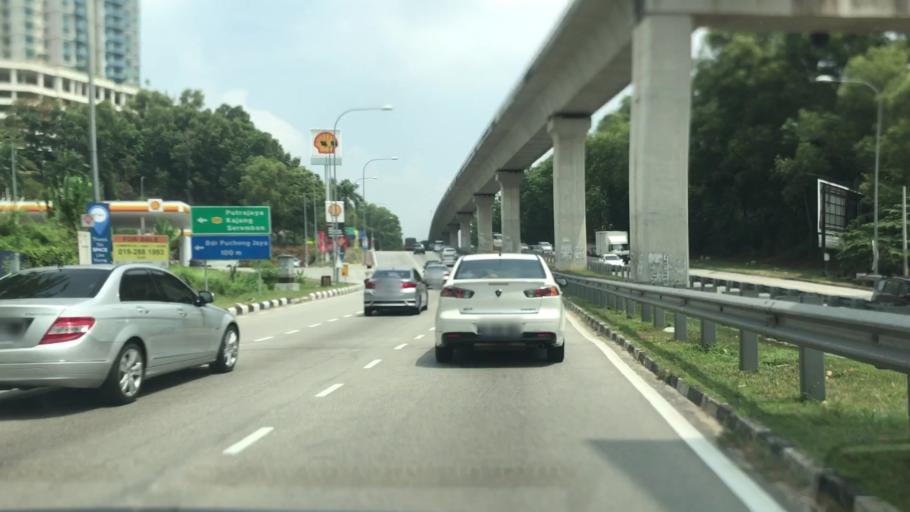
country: MY
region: Selangor
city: Subang Jaya
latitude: 3.0494
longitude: 101.6342
